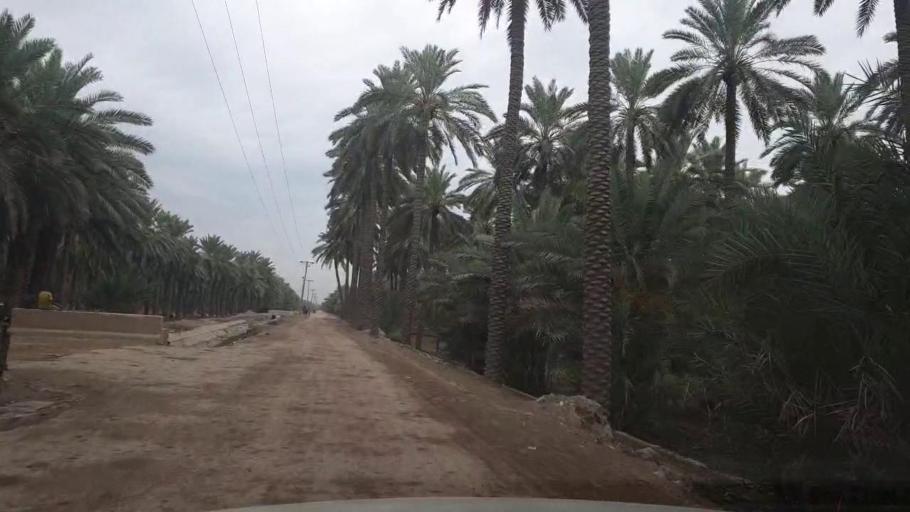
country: PK
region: Sindh
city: Sukkur
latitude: 27.6149
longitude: 68.8181
